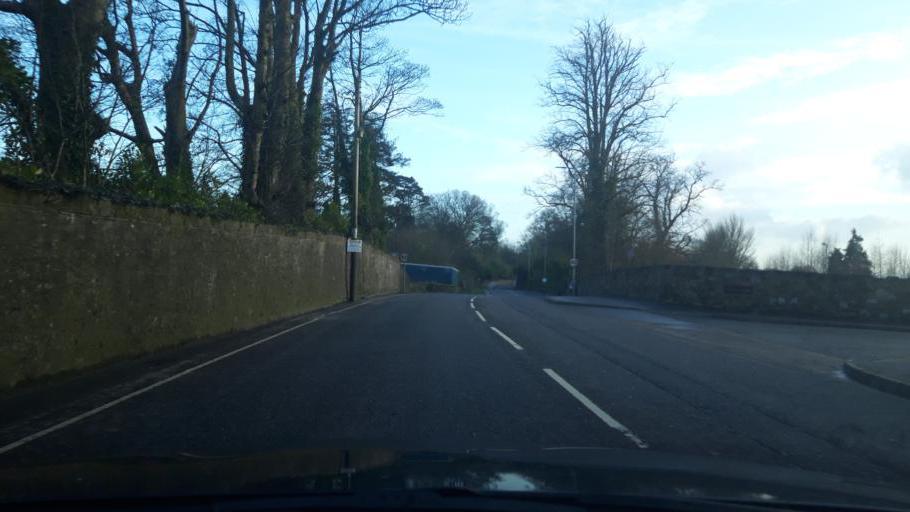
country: GB
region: Northern Ireland
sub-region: Dungannon District
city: Dungannon
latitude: 54.4981
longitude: -6.7615
